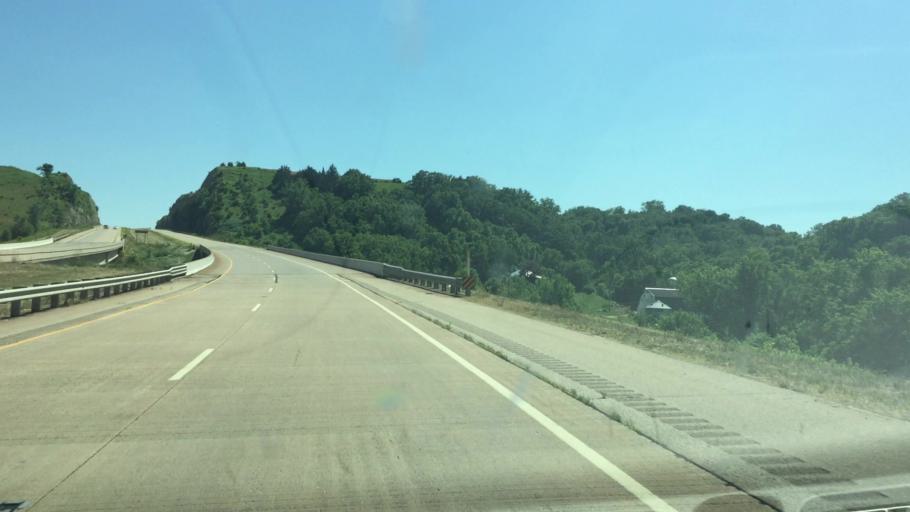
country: US
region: Wisconsin
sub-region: Grant County
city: Dickeyville
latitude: 42.6449
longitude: -90.5766
